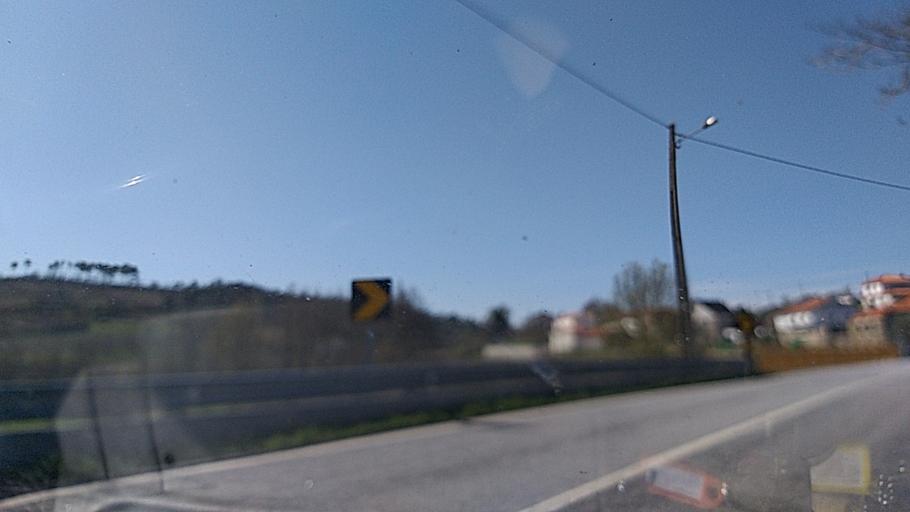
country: PT
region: Guarda
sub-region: Celorico da Beira
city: Celorico da Beira
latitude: 40.5927
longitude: -7.4355
